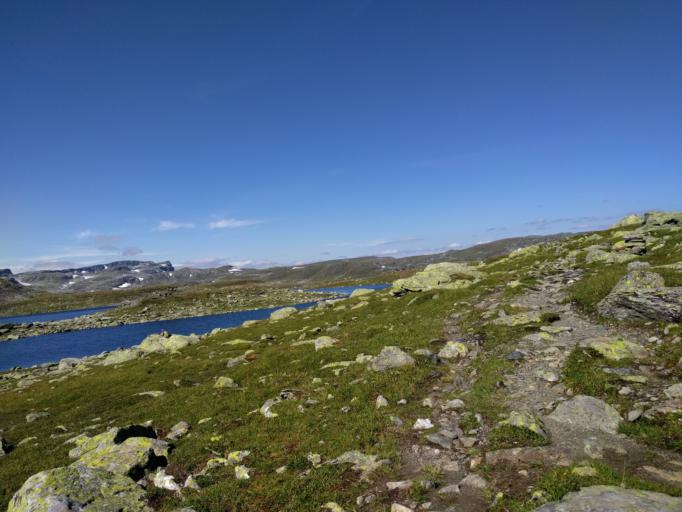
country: NO
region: Aust-Agder
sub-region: Bykle
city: Hovden
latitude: 59.8878
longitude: 7.2071
